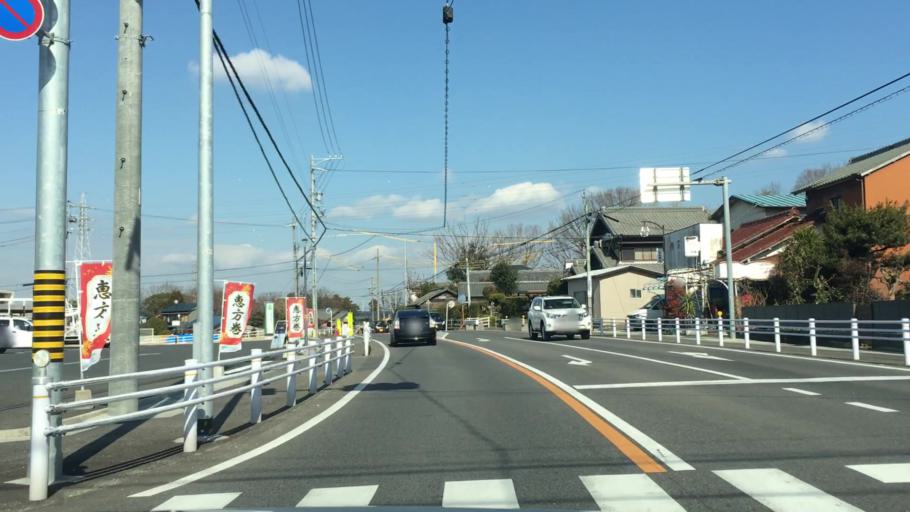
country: JP
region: Aichi
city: Anjo
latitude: 35.0152
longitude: 137.1228
